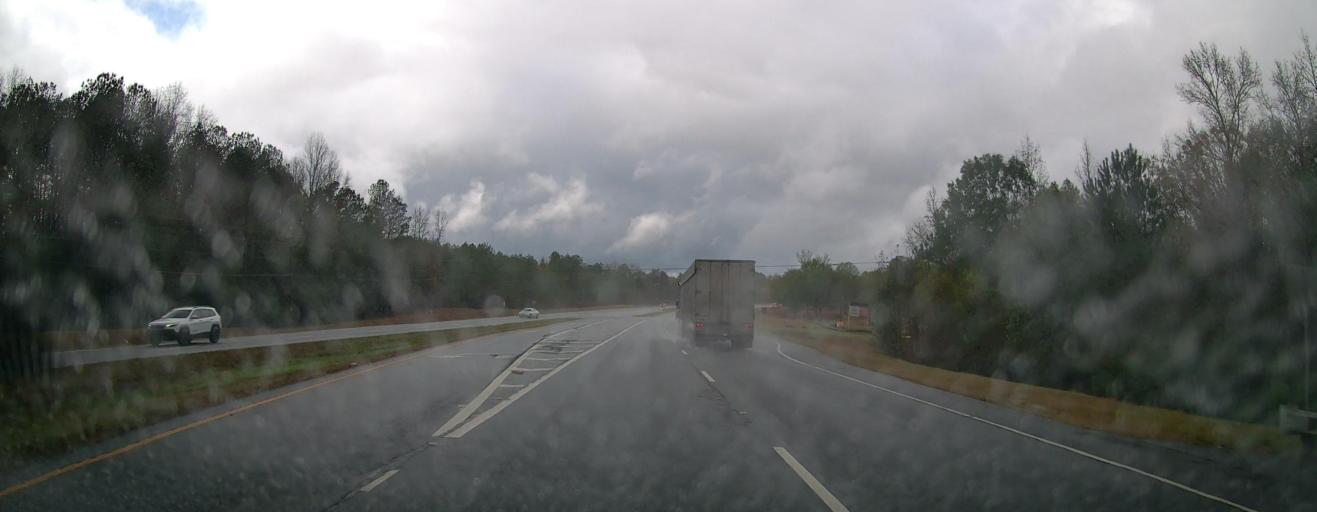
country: US
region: Georgia
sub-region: Clarke County
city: Country Club Estates
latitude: 34.0261
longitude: -83.3995
